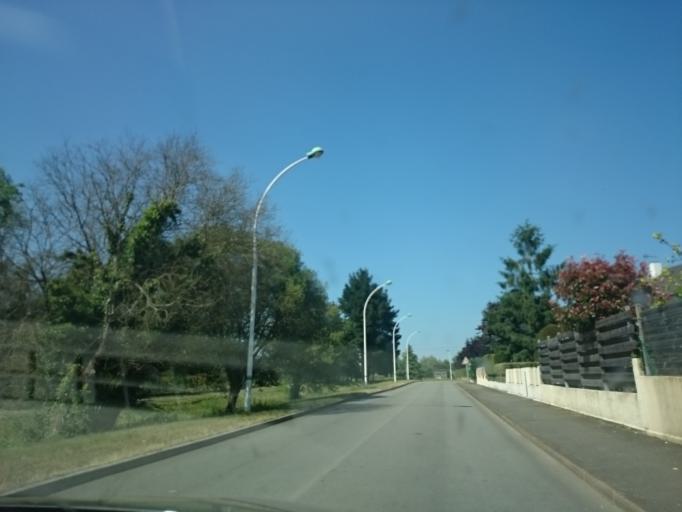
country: FR
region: Pays de la Loire
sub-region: Departement de la Loire-Atlantique
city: Indre
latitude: 47.2021
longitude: -1.6744
